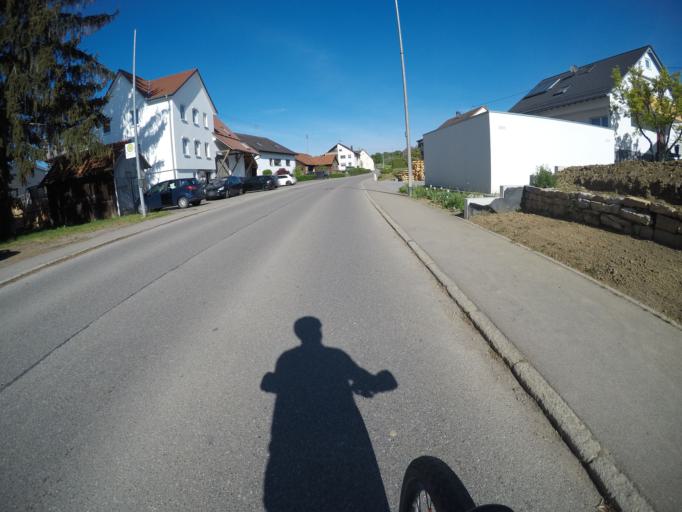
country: DE
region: Baden-Wuerttemberg
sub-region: Tuebingen Region
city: Pliezhausen
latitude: 48.5895
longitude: 9.1742
